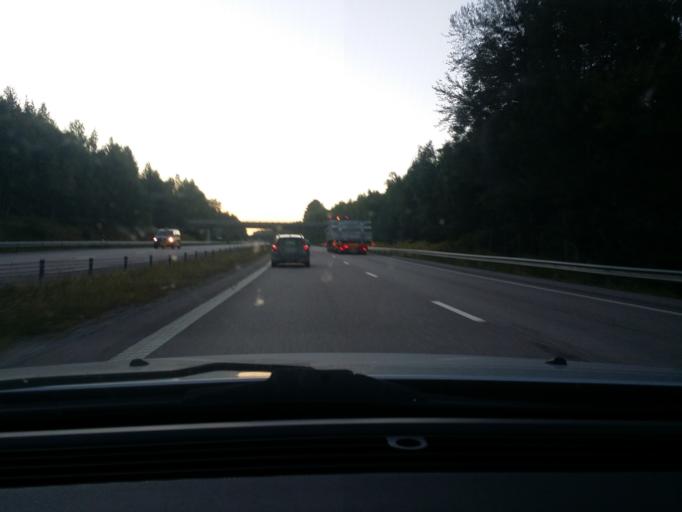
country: SE
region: Uppsala
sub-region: Enkopings Kommun
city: Enkoping
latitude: 59.6524
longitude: 17.1017
